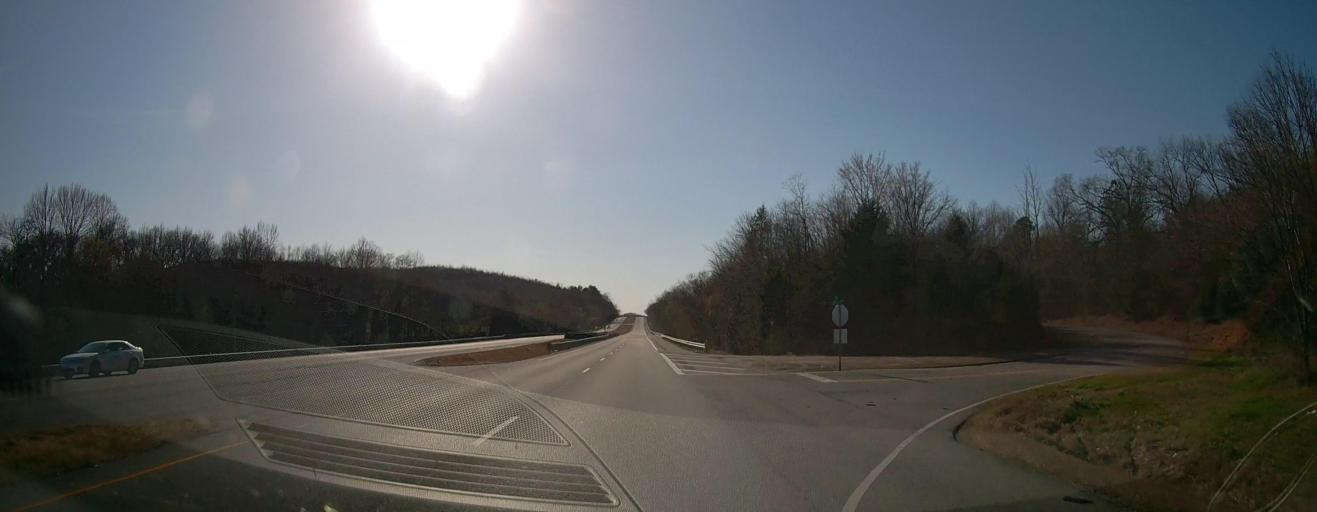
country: US
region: Alabama
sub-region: Colbert County
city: Cherokee
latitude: 34.7625
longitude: -88.0312
